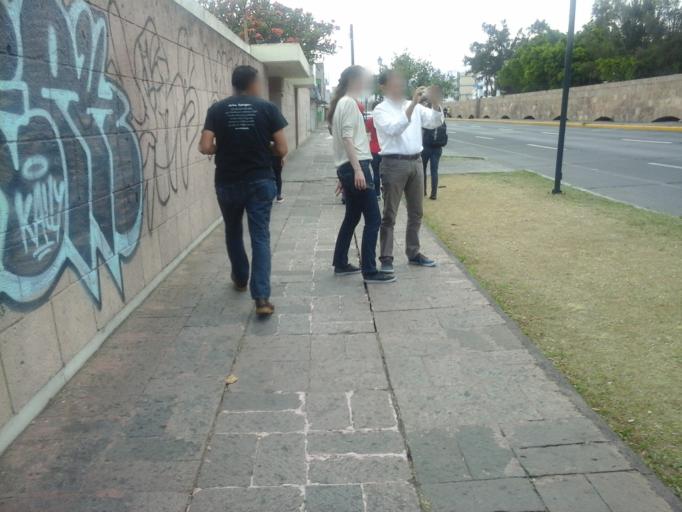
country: MX
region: Michoacan
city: Morelia
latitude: 19.6971
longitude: -101.1710
